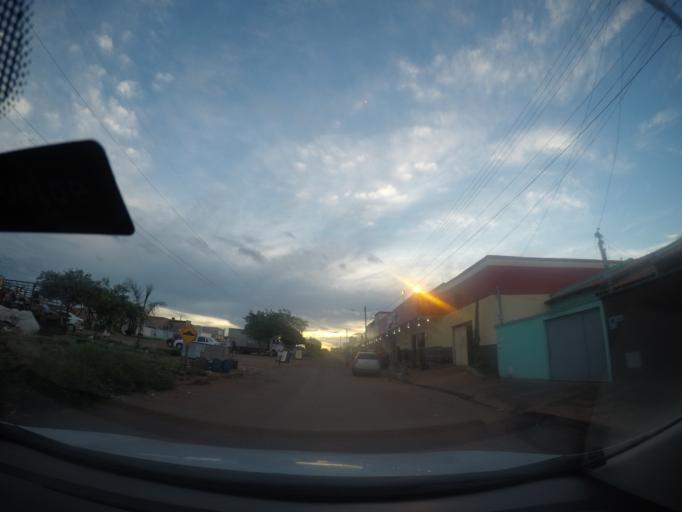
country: BR
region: Goias
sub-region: Goianira
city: Goianira
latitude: -16.5717
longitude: -49.3845
